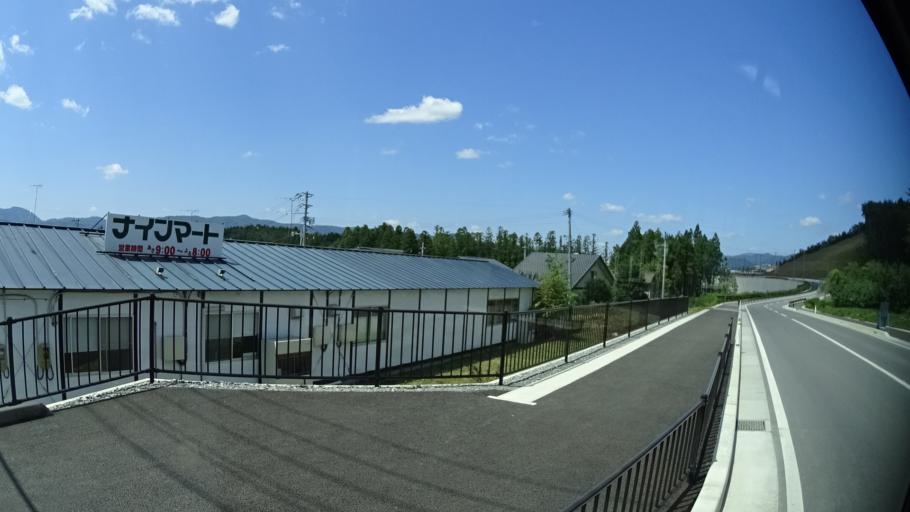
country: JP
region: Iwate
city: Ofunato
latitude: 39.0233
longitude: 141.6484
